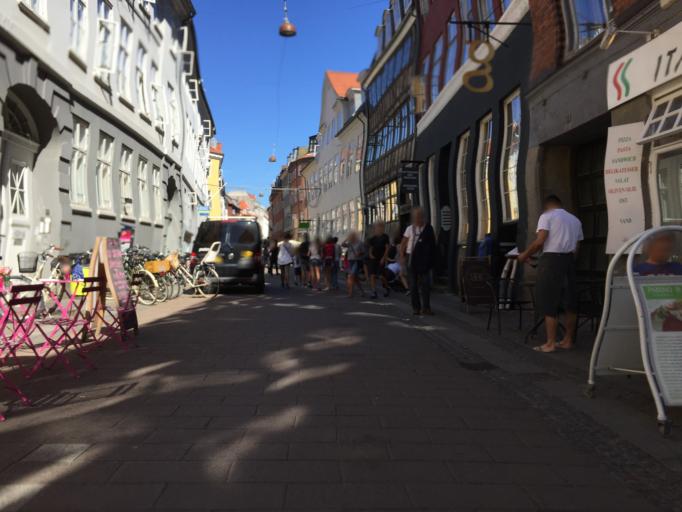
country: DK
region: Capital Region
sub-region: Kobenhavn
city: Copenhagen
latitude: 55.6768
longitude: 12.5747
